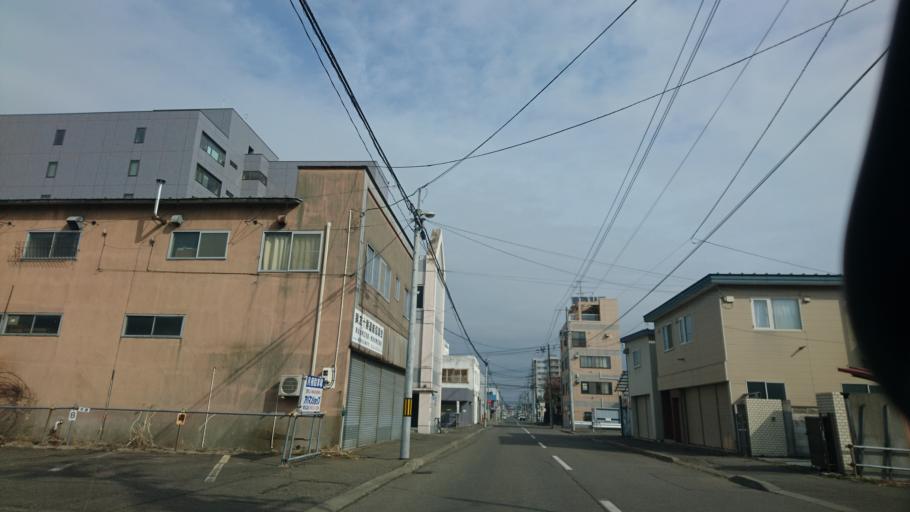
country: JP
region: Hokkaido
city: Obihiro
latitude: 42.9220
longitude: 143.2062
